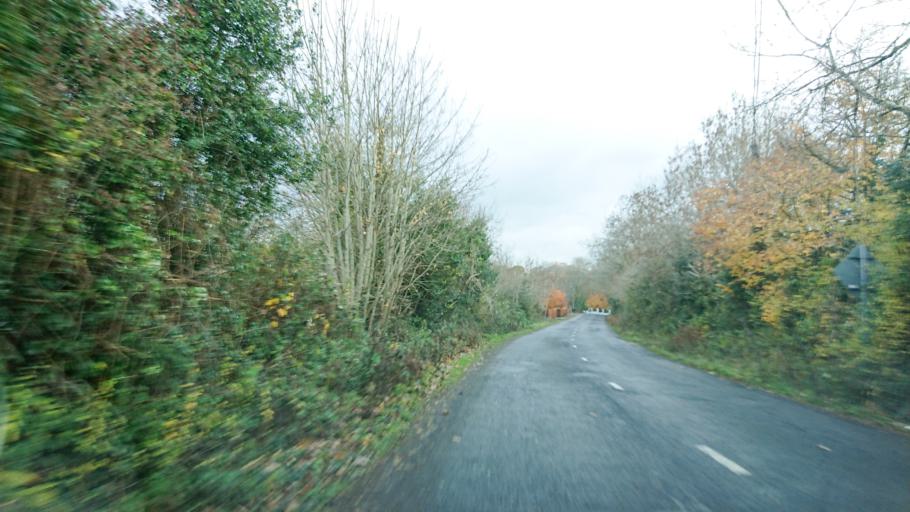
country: IE
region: Munster
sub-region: South Tipperary
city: Cluain Meala
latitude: 52.3533
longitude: -7.6456
